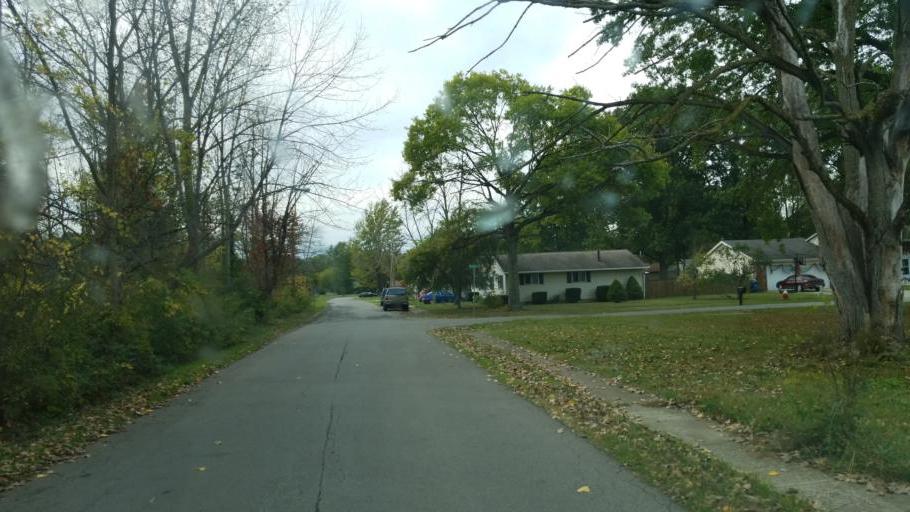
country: US
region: Ohio
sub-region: Lorain County
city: Sheffield Lake
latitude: 41.4792
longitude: -82.1171
